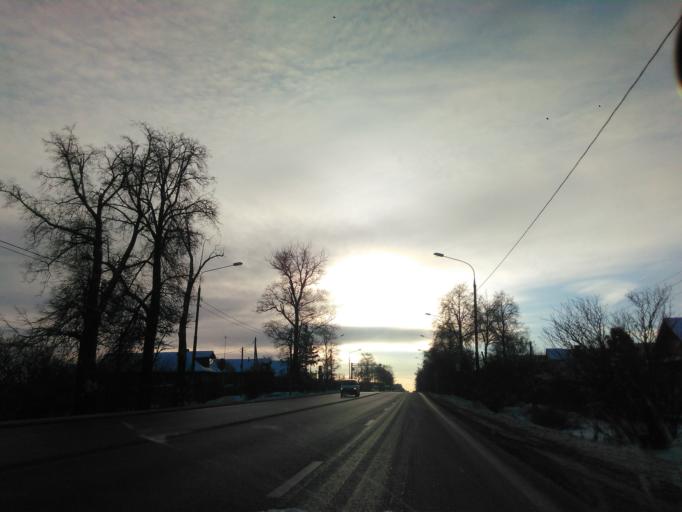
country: RU
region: Moskovskaya
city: Spas-Zaulok
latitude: 56.4705
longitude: 36.5818
